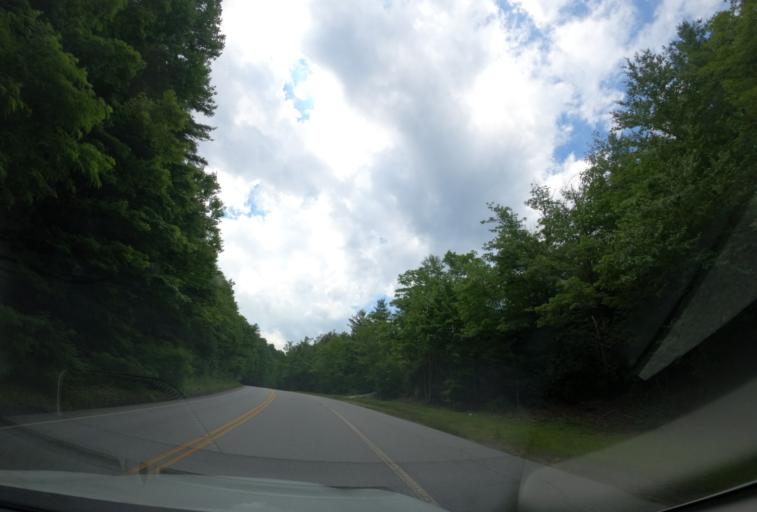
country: US
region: South Carolina
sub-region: Oconee County
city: Walhalla
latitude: 35.0329
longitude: -83.0178
